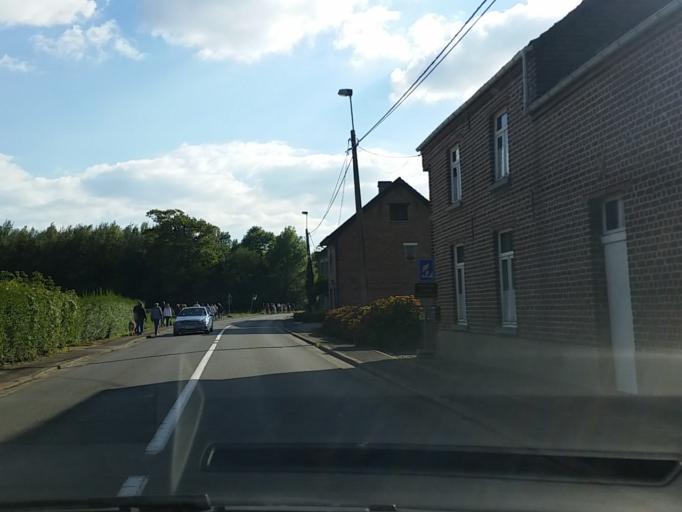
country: BE
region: Flanders
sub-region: Provincie Vlaams-Brabant
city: Herent
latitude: 50.9208
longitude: 4.6146
